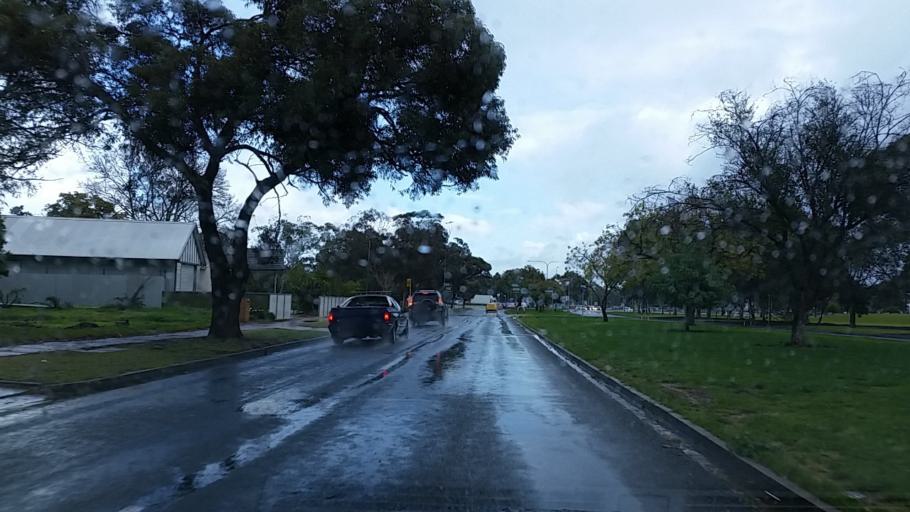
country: AU
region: South Australia
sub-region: Salisbury
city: Elizabeth
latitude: -34.7191
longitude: 138.6757
